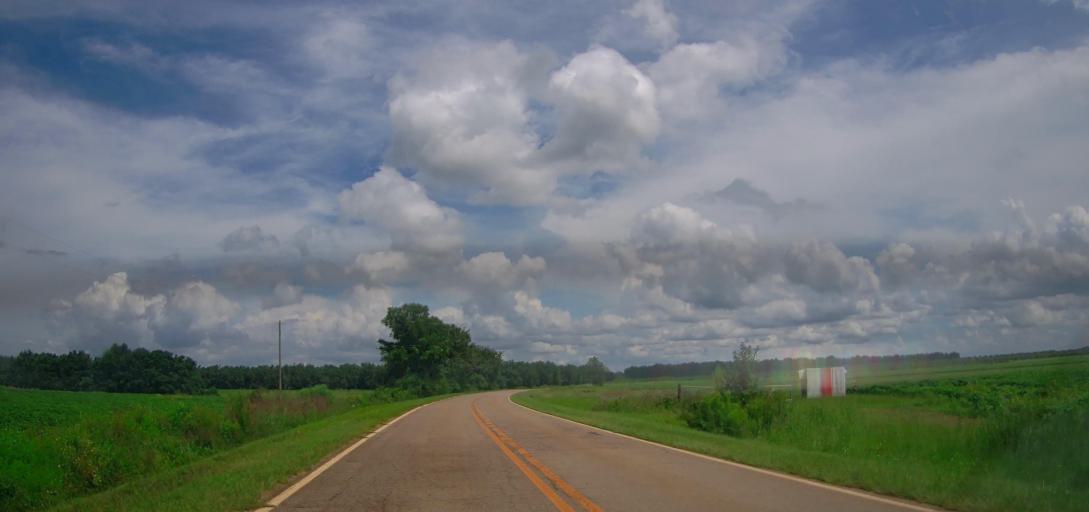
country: US
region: Georgia
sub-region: Houston County
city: Perry
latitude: 32.5218
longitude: -83.7690
